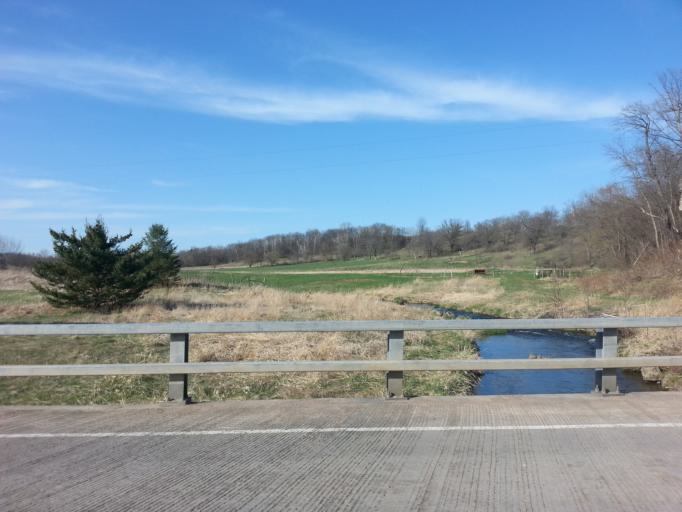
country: US
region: Wisconsin
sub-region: Pierce County
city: Ellsworth
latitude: 44.7205
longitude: -92.5778
